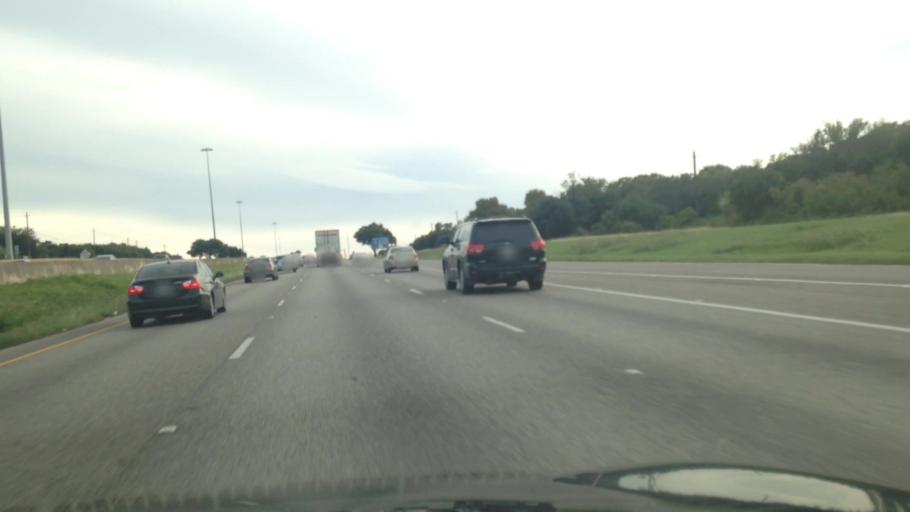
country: US
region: Texas
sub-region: Travis County
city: Onion Creek
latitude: 30.1301
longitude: -97.8001
